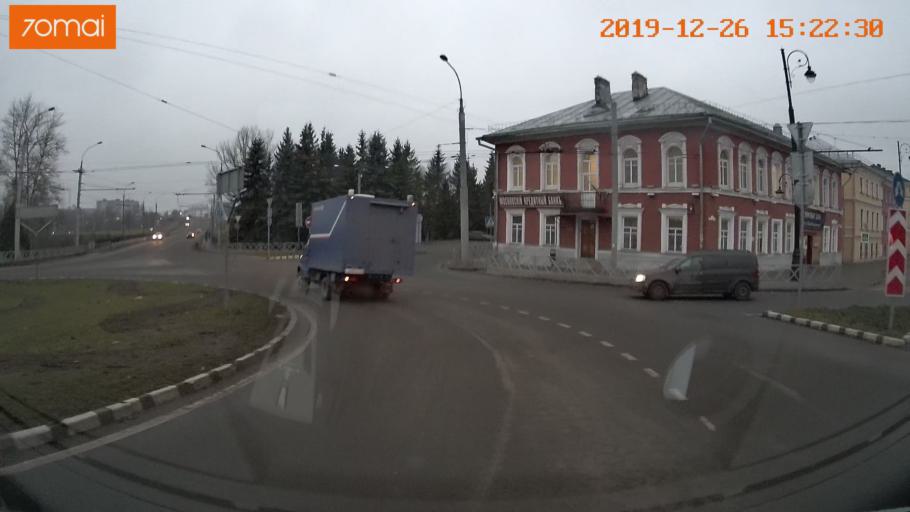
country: RU
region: Jaroslavl
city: Rybinsk
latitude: 58.0478
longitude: 38.8599
